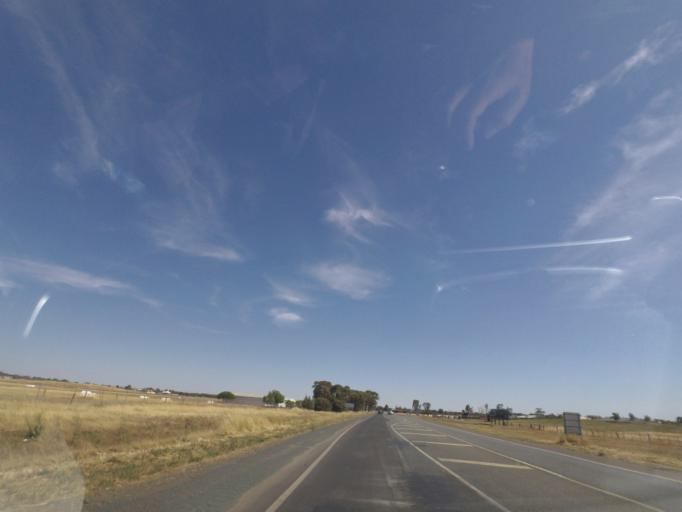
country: AU
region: Victoria
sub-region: Greater Shepparton
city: Shepparton
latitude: -36.4285
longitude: 145.3894
